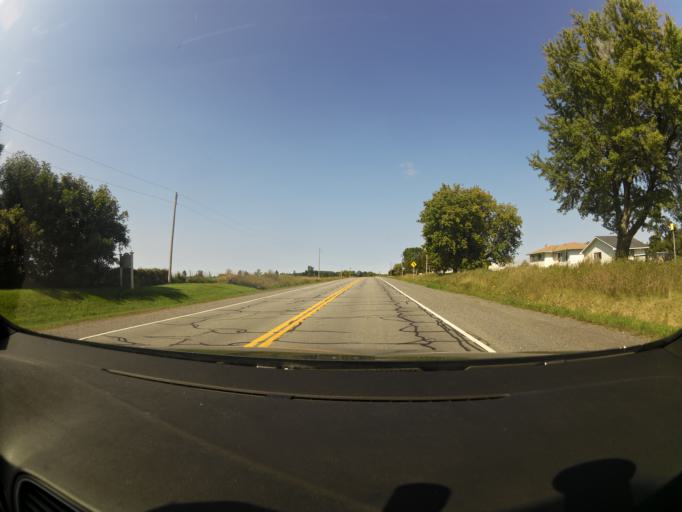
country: CA
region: Ontario
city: Arnprior
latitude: 45.3428
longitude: -76.2914
